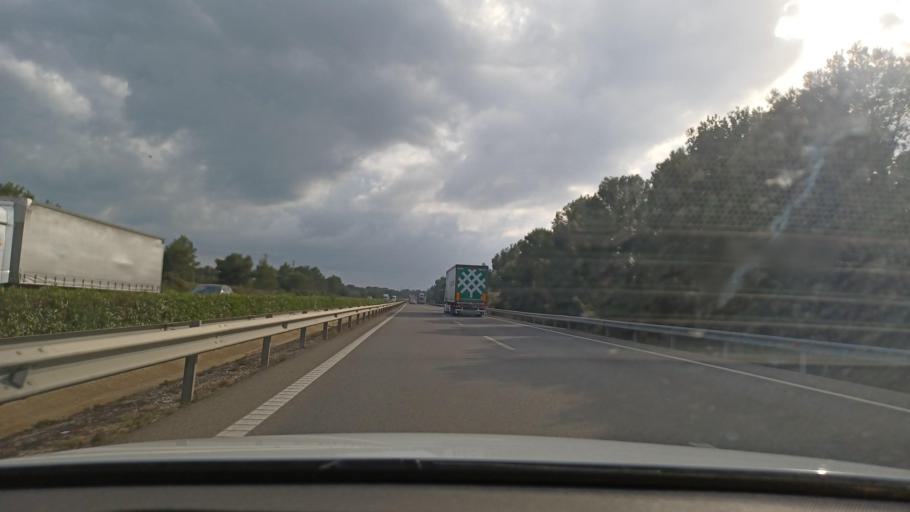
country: ES
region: Catalonia
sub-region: Provincia de Tarragona
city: l'Ametlla de Mar
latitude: 40.9175
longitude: 0.8293
